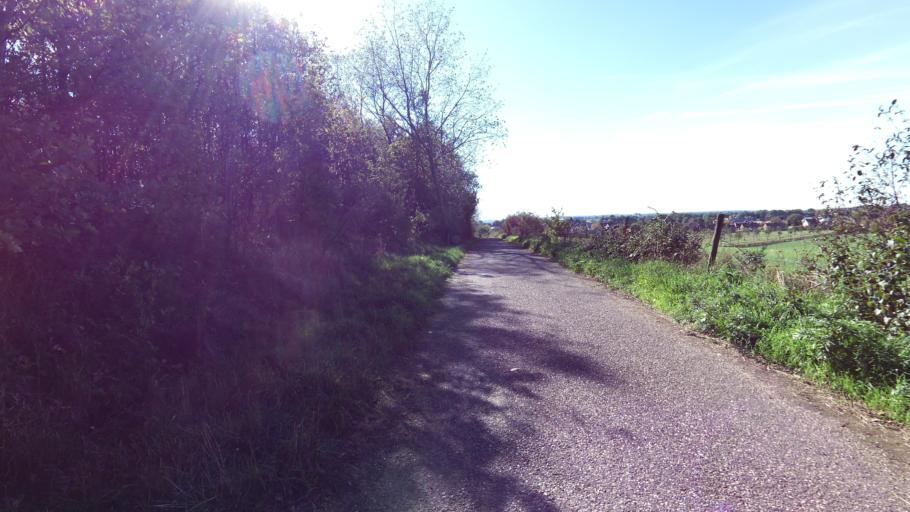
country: NL
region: Limburg
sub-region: Gemeente Simpelveld
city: Simpelveld
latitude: 50.8220
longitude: 6.0171
